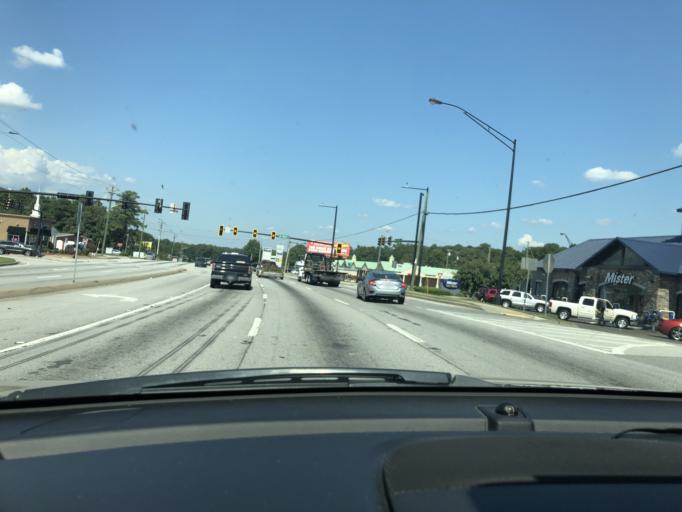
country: US
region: Georgia
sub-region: Gwinnett County
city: Mountain Park
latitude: 33.8267
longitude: -84.0972
